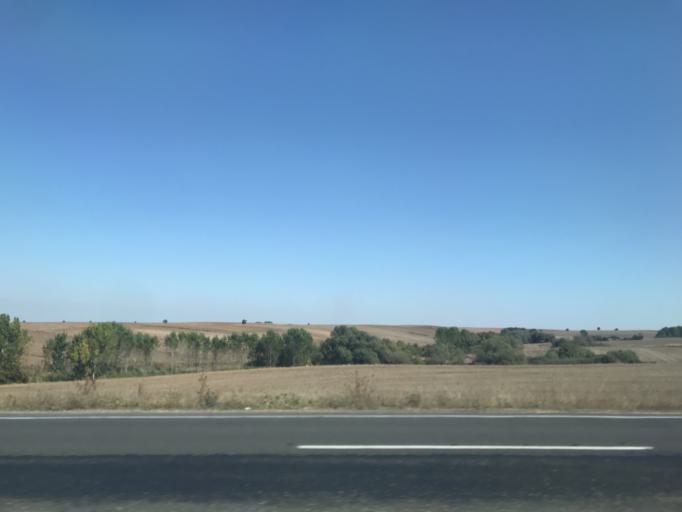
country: TR
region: Tekirdag
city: Muratli
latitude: 41.1171
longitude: 27.4899
